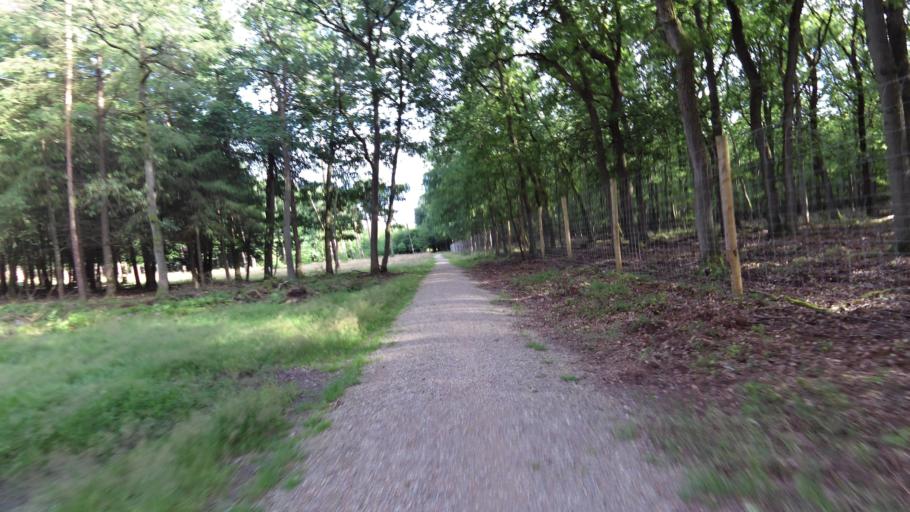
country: NL
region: Gelderland
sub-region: Gemeente Apeldoorn
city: Uddel
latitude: 52.2252
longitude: 5.8656
